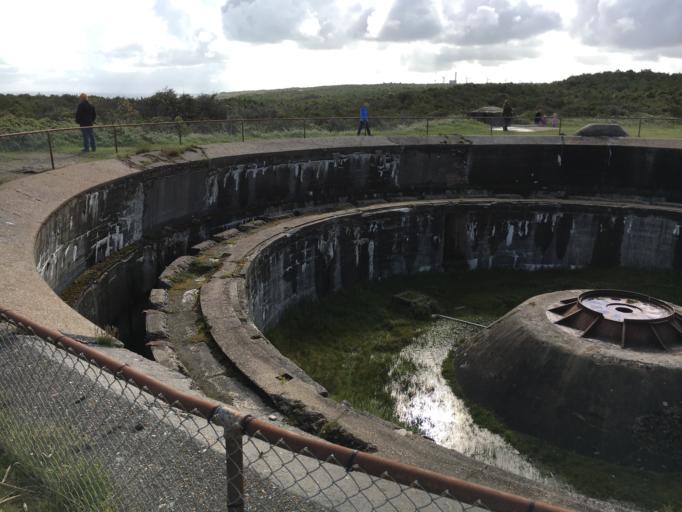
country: DK
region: North Denmark
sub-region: Thisted Kommune
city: Hanstholm
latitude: 57.1219
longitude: 8.6125
